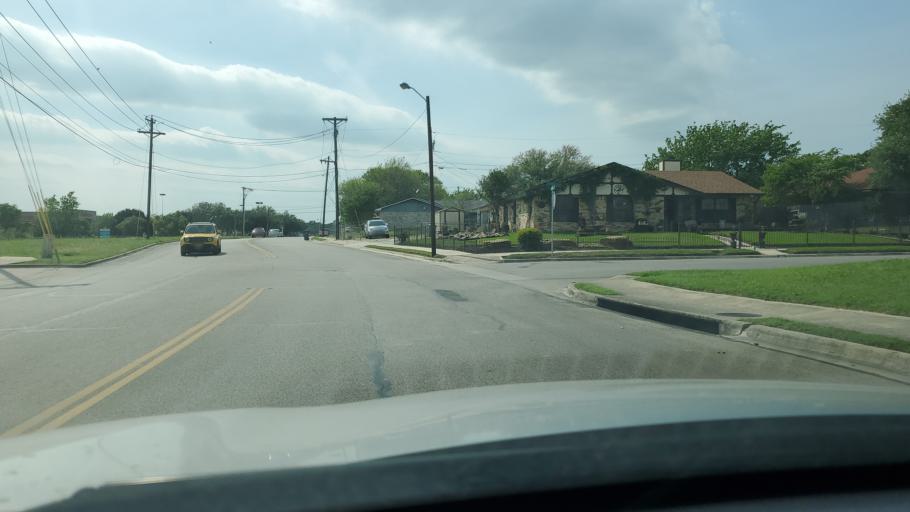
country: US
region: Texas
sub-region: Bell County
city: Killeen
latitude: 31.0934
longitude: -97.7120
